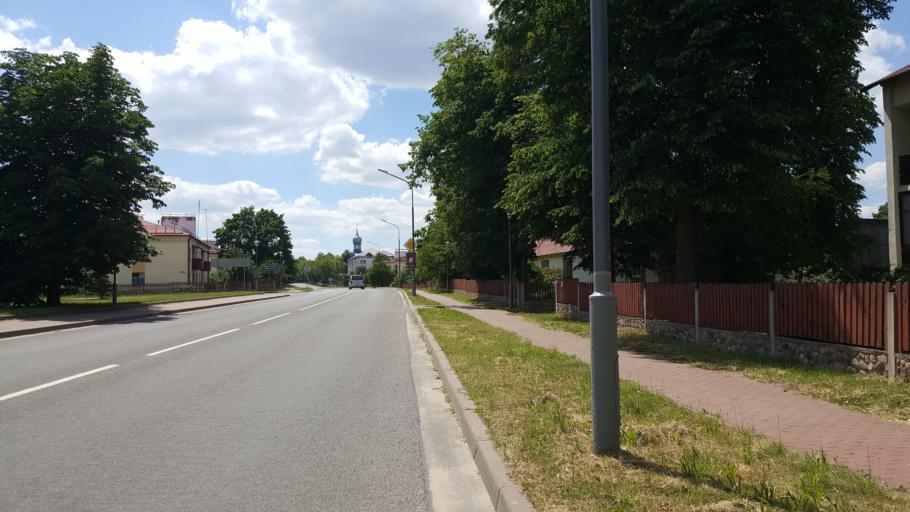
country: BY
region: Brest
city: Kamyanyuki
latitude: 52.5618
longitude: 23.7995
